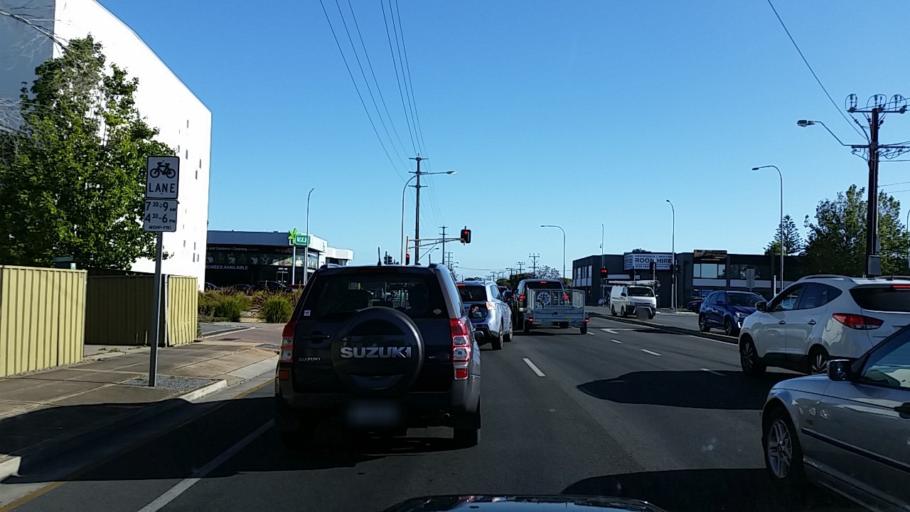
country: AU
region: South Australia
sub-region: City of West Torrens
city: Plympton
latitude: -34.9321
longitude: 138.5525
